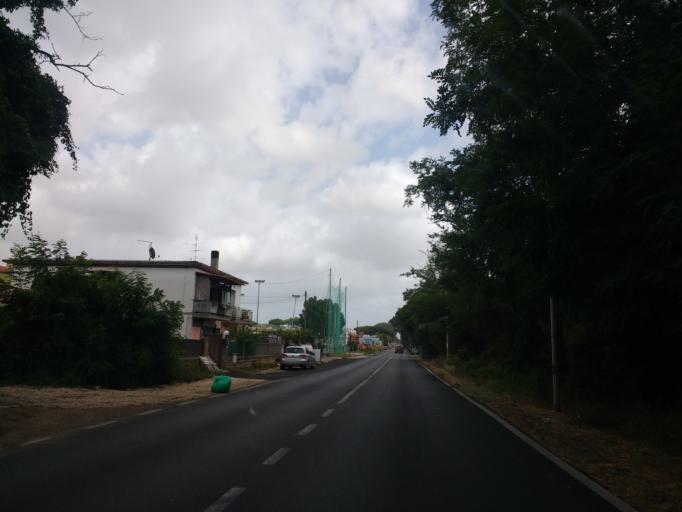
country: IT
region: Latium
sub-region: Citta metropolitana di Roma Capitale
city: Lavinio
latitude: 41.4922
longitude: 12.5950
